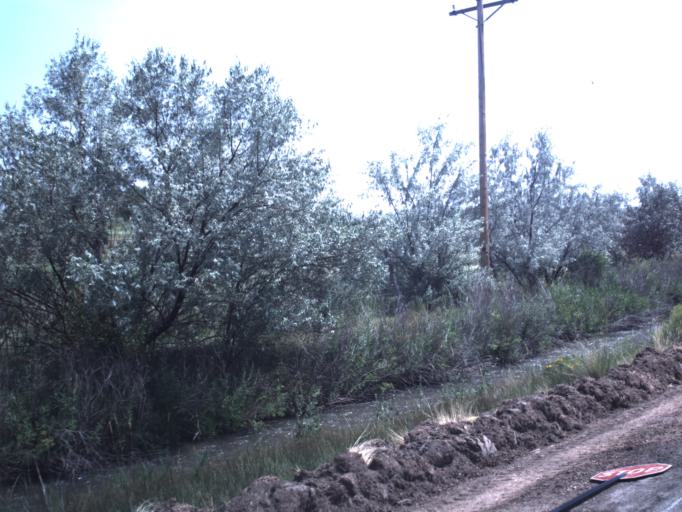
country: US
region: Utah
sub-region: Duchesne County
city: Roosevelt
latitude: 40.4055
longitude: -110.0298
